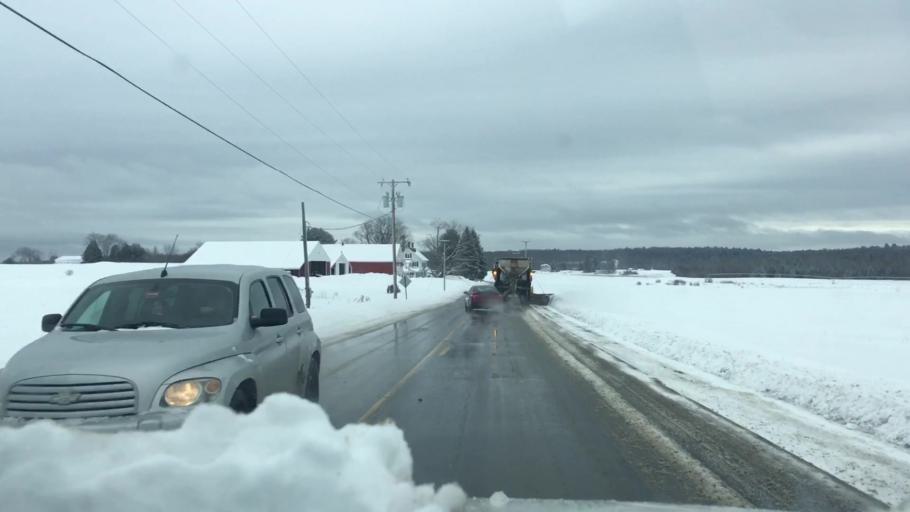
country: US
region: Maine
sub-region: Penobscot County
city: Garland
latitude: 44.9774
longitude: -69.0986
